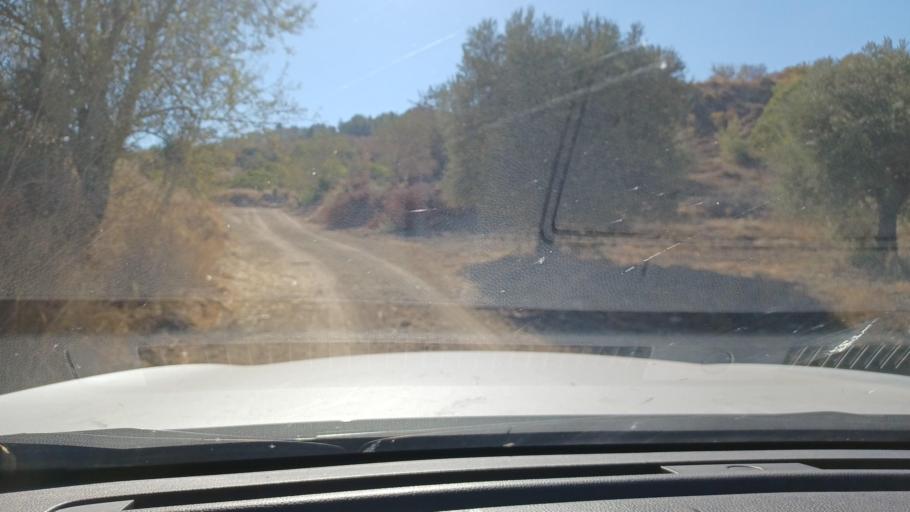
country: CY
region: Pafos
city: Polis
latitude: 35.0080
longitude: 32.5095
